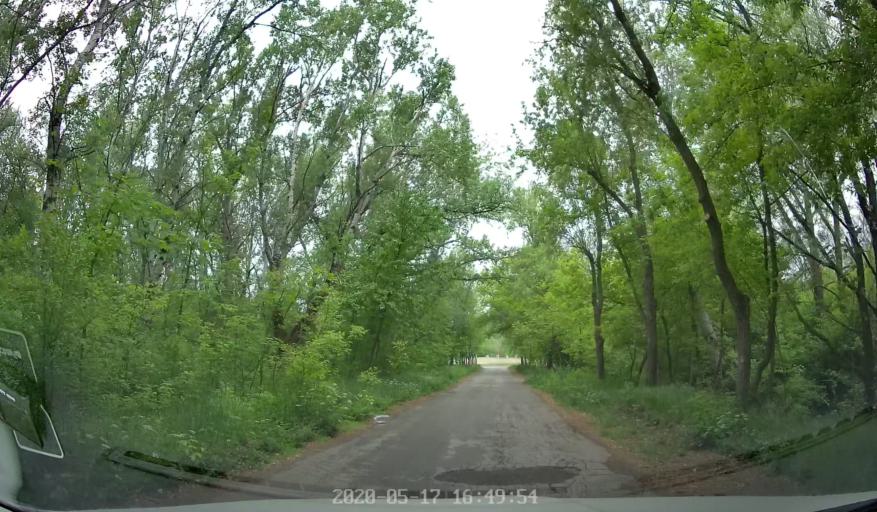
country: MD
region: Chisinau
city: Vatra
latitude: 47.0522
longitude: 28.7852
